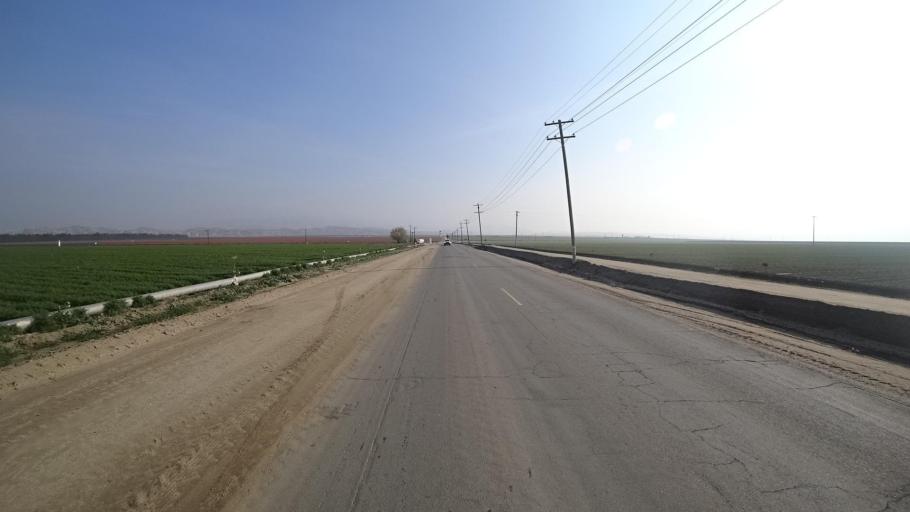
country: US
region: California
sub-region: Kern County
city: Arvin
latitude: 35.0928
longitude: -118.8527
